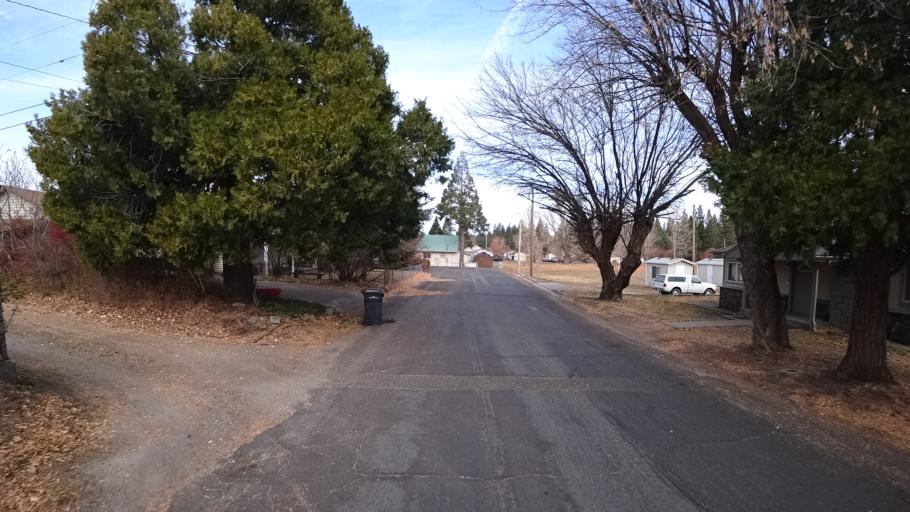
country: US
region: California
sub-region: Siskiyou County
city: Weed
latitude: 41.4374
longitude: -122.3775
